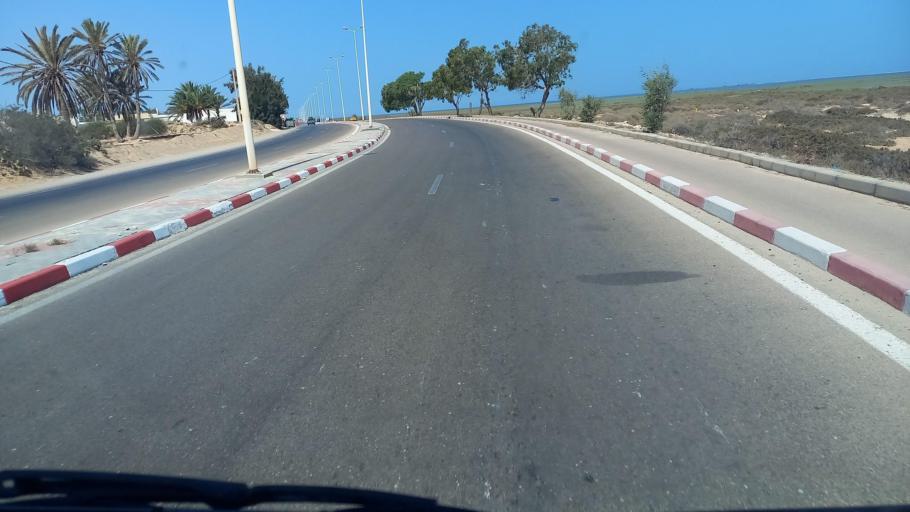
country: TN
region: Madanin
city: Houmt Souk
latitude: 33.8718
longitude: 10.9353
